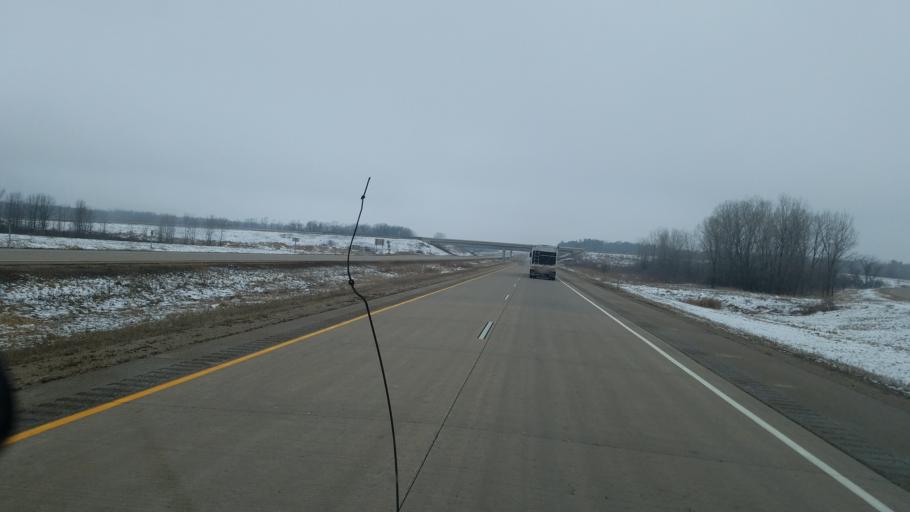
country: US
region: Wisconsin
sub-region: Winnebago County
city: Winneconne
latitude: 44.2344
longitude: -88.7341
